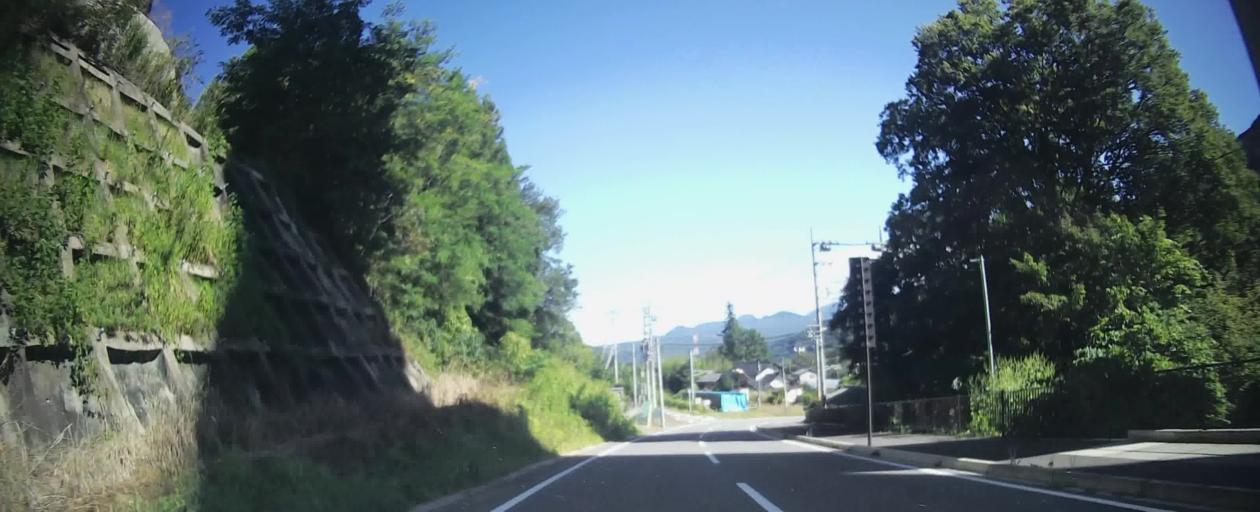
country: JP
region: Gunma
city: Nakanojomachi
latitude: 36.5736
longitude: 138.7354
